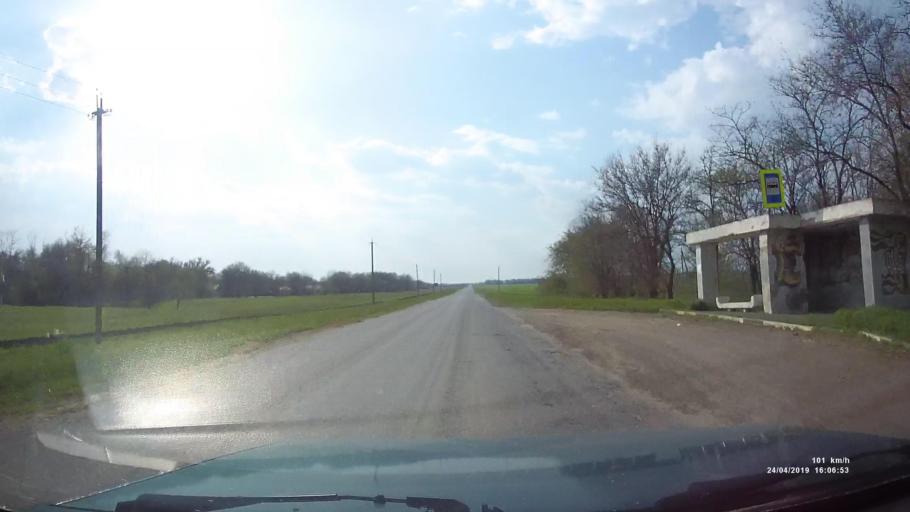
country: RU
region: Rostov
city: Sovetskoye
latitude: 46.6894
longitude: 42.3398
